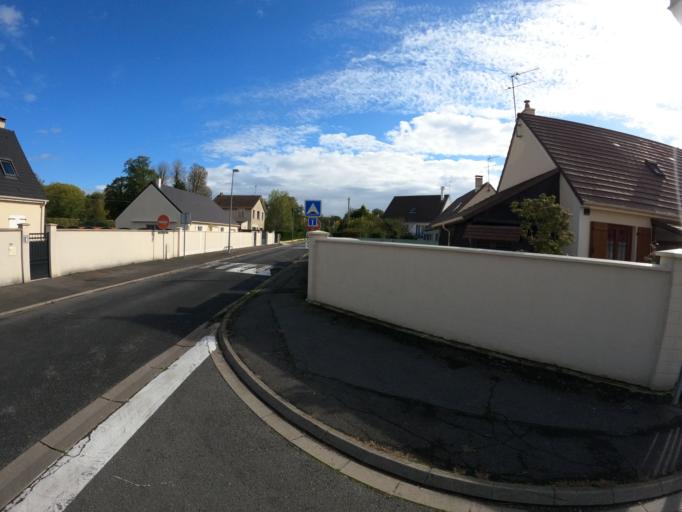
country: FR
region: Ile-de-France
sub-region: Departement de Seine-et-Marne
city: Saint-Germain-sur-Morin
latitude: 48.8846
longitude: 2.8512
